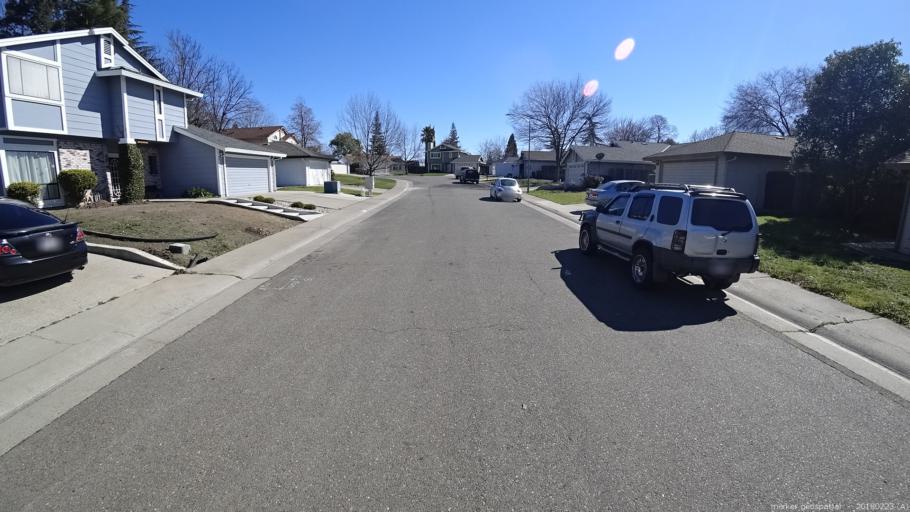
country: US
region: California
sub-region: Sacramento County
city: North Highlands
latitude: 38.7169
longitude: -121.3780
